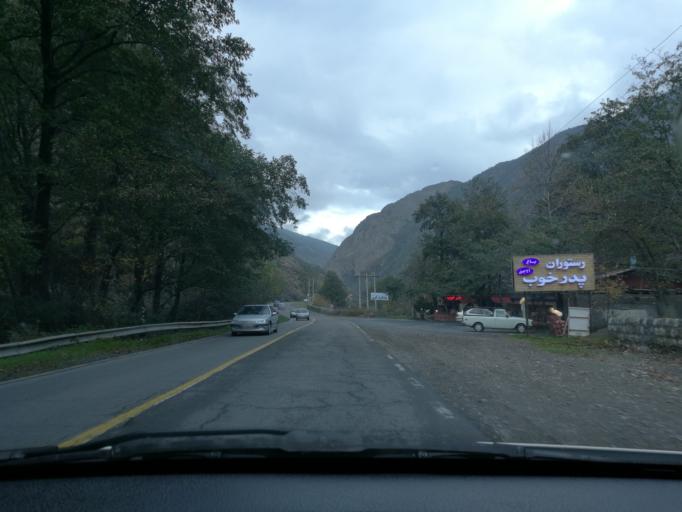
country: IR
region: Mazandaran
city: Chalus
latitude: 36.3529
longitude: 51.2611
